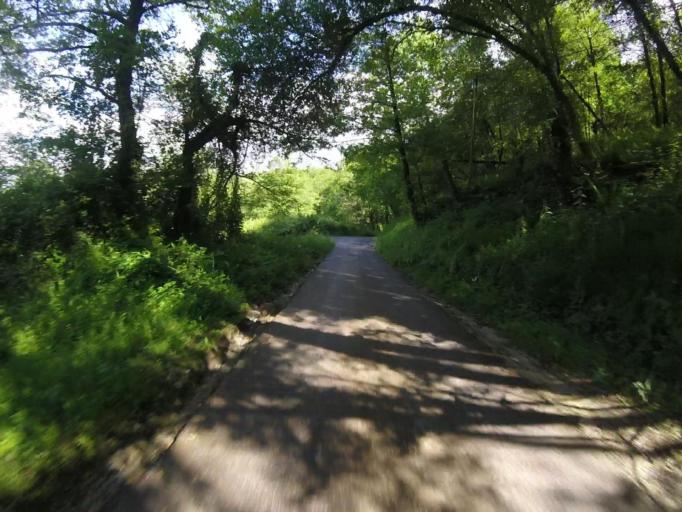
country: ES
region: Basque Country
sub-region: Provincia de Guipuzcoa
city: Errenteria
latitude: 43.2916
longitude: -1.9099
